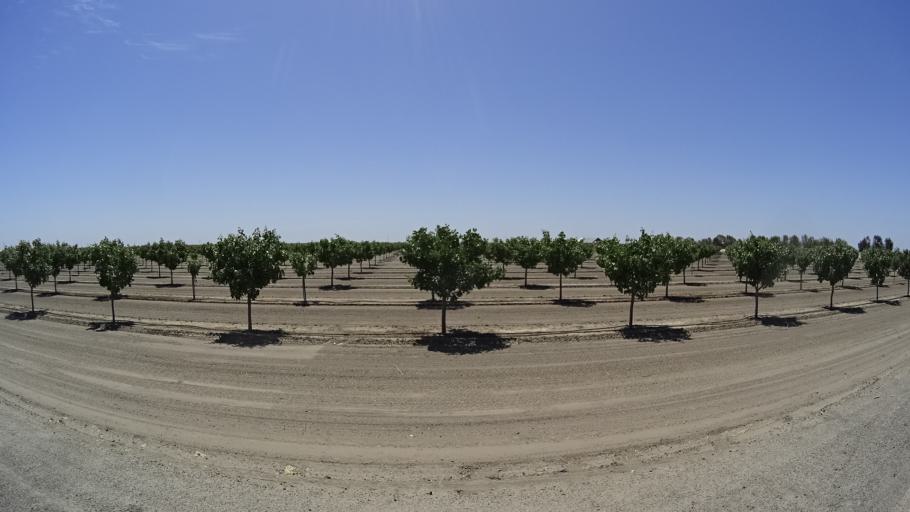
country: US
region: California
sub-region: Kings County
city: Corcoran
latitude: 36.1162
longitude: -119.6311
